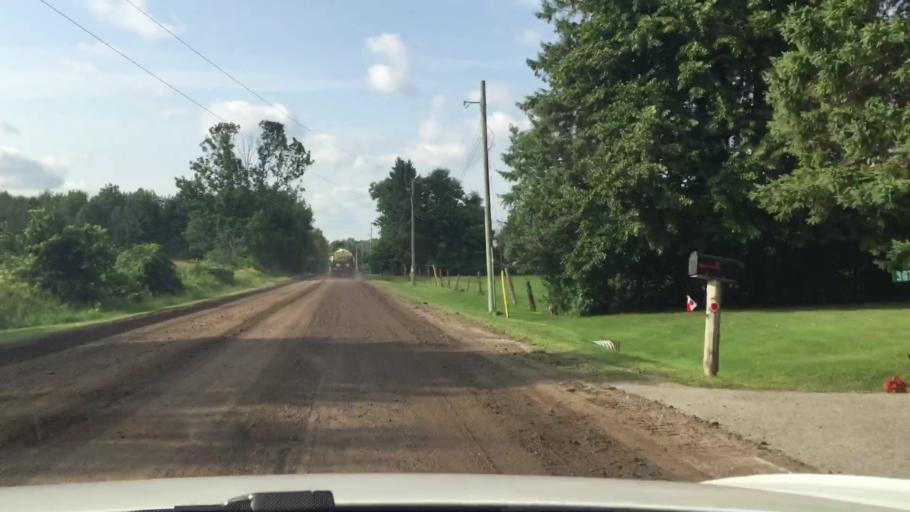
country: CA
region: Ontario
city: Oshawa
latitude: 43.9383
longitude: -78.7466
